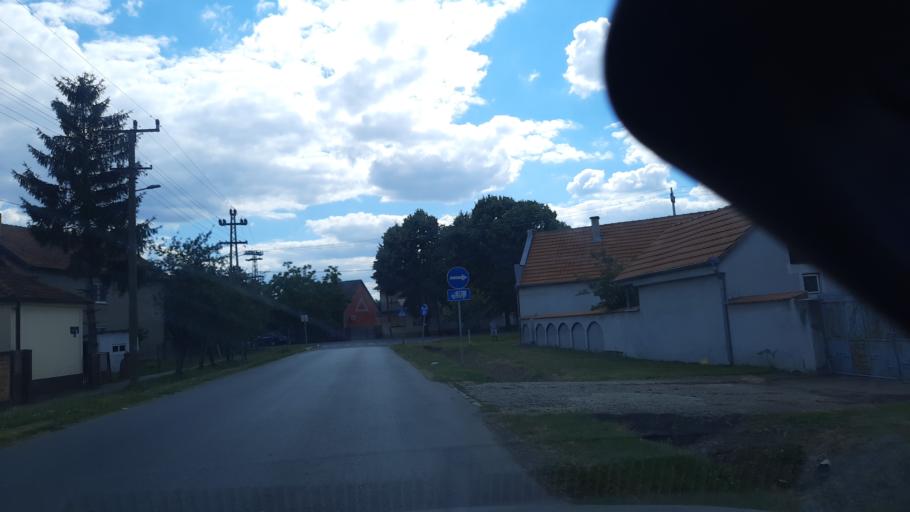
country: RS
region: Autonomna Pokrajina Vojvodina
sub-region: Sremski Okrug
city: Pecinci
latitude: 44.9139
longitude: 19.9656
